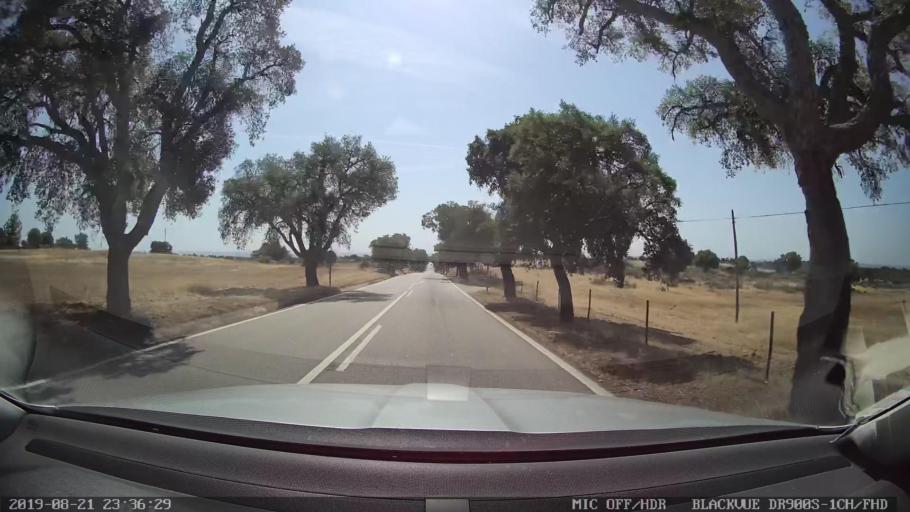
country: PT
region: Guarda
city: Alcains
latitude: 39.8754
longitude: -7.3740
